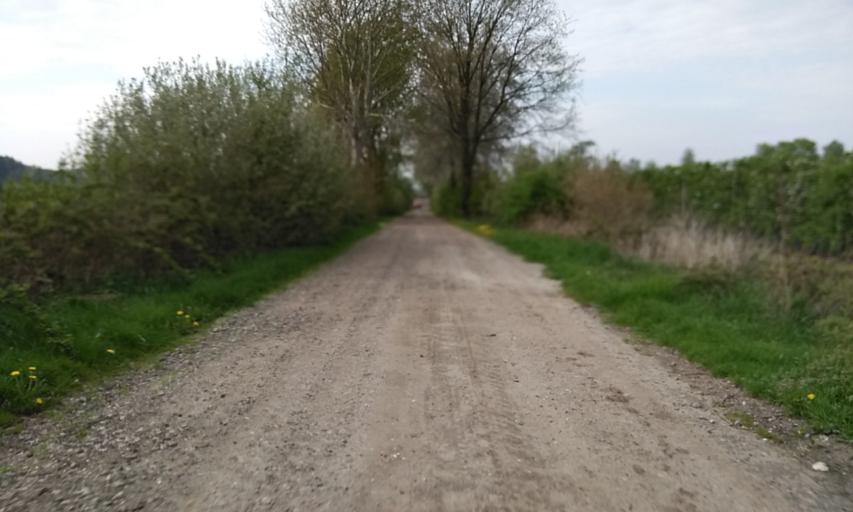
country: DE
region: Lower Saxony
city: Bliedersdorf
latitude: 53.4627
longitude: 9.5581
